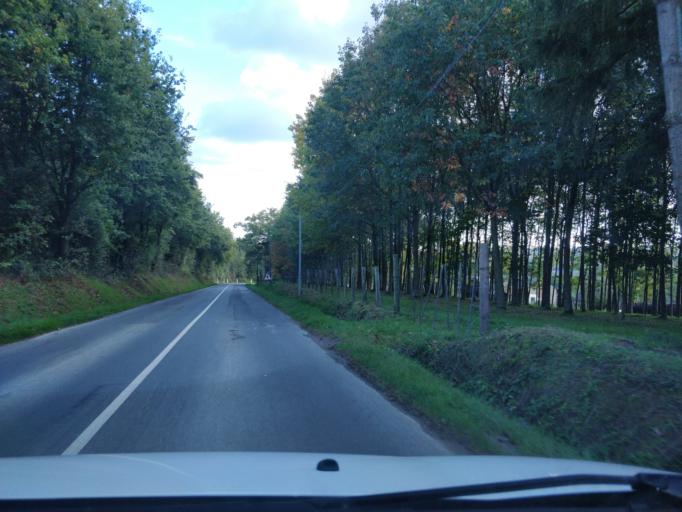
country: FR
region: Brittany
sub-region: Departement d'Ille-et-Vilaine
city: La Bouexiere
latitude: 48.1988
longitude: -1.4237
